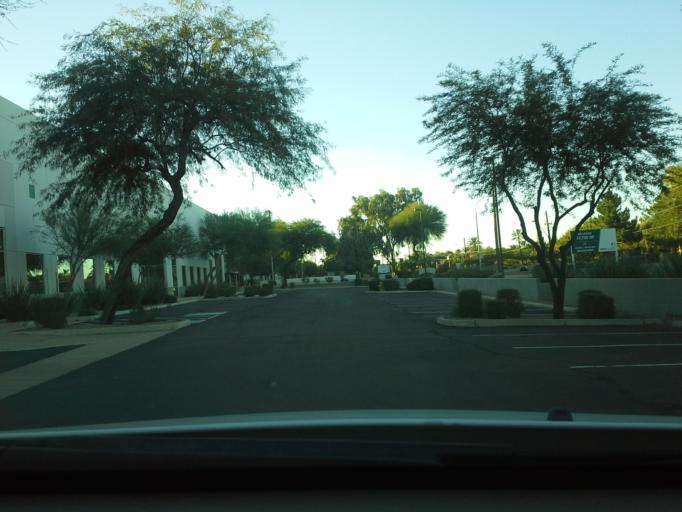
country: US
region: Arizona
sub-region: Maricopa County
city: Guadalupe
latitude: 33.3572
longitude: -111.9455
